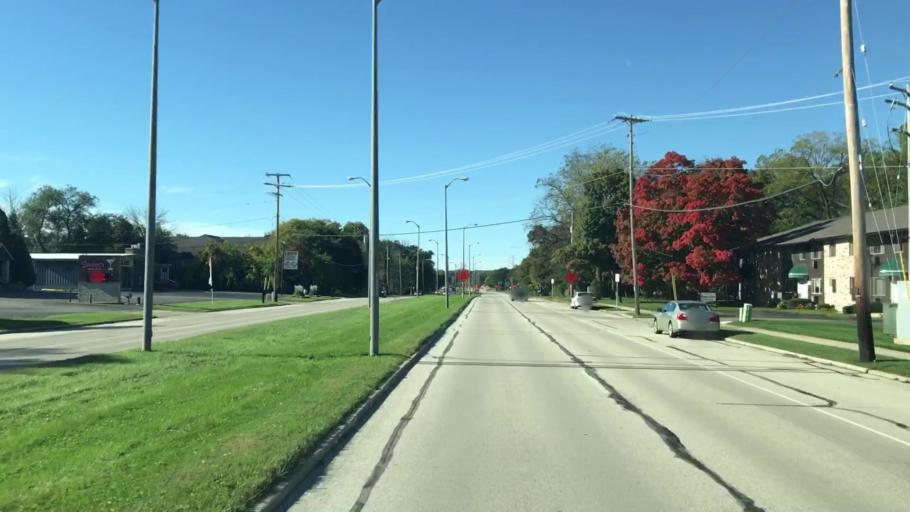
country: US
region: Wisconsin
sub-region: Milwaukee County
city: Hales Corners
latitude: 42.9430
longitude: -88.0388
